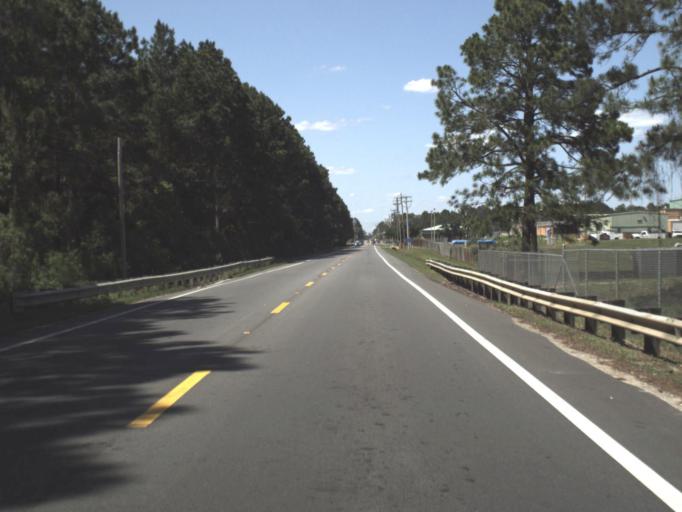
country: US
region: Florida
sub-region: Bay County
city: Hiland Park
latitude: 30.2069
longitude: -85.6077
